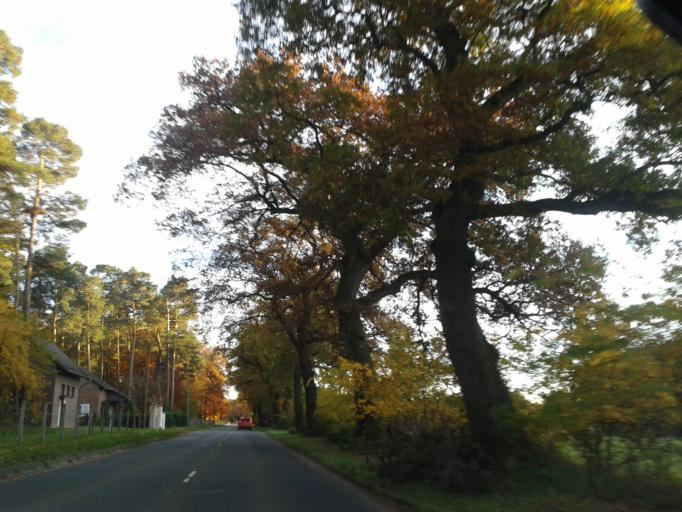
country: DE
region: North Rhine-Westphalia
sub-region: Regierungsbezirk Detmold
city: Paderborn
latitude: 51.7663
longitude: 8.7594
